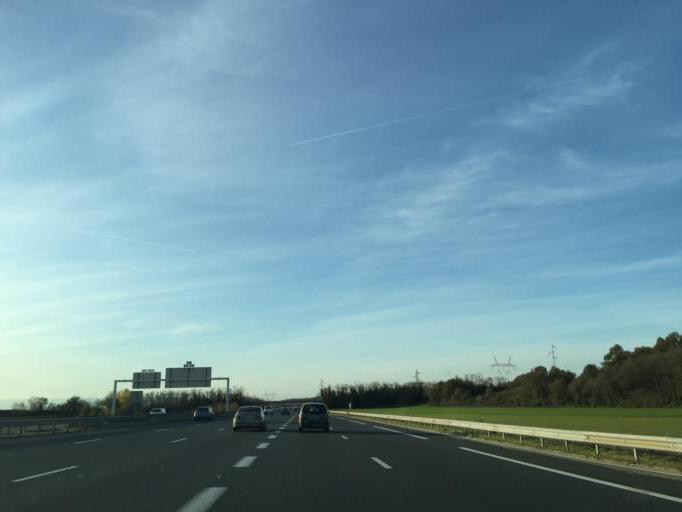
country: FR
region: Rhone-Alpes
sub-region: Departement du Rhone
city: Saint-Laurent-de-Mure
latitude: 45.6725
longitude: 5.0424
